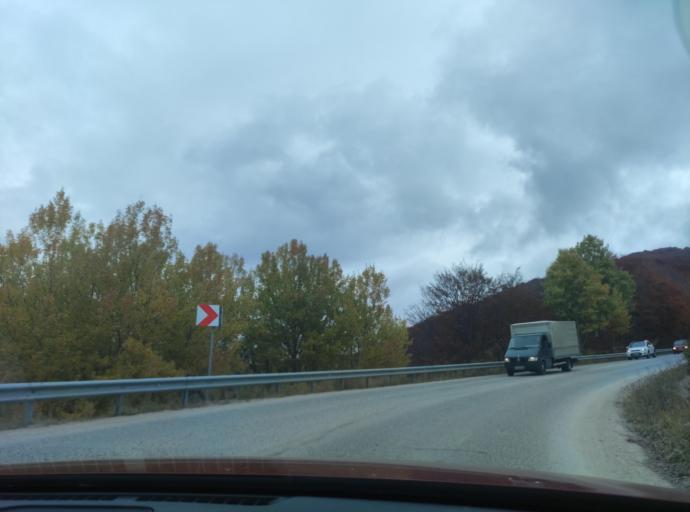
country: BG
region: Sofiya
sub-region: Obshtina Godech
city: Godech
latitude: 43.1131
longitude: 23.1099
